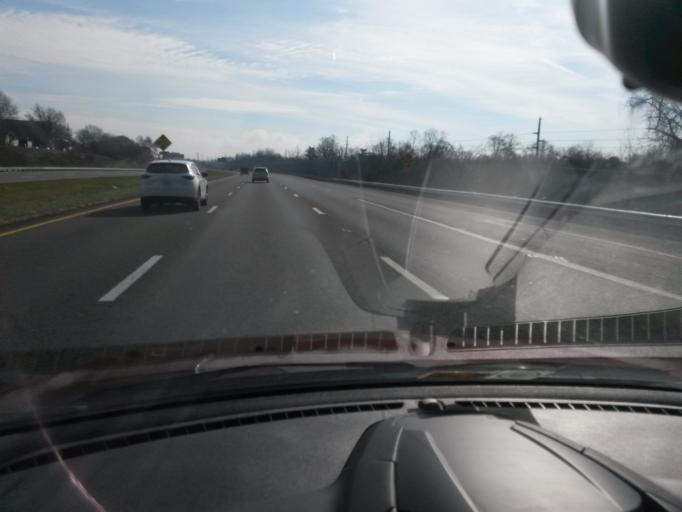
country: US
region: Virginia
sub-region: Roanoke County
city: Hollins
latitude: 37.3061
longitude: -79.9712
